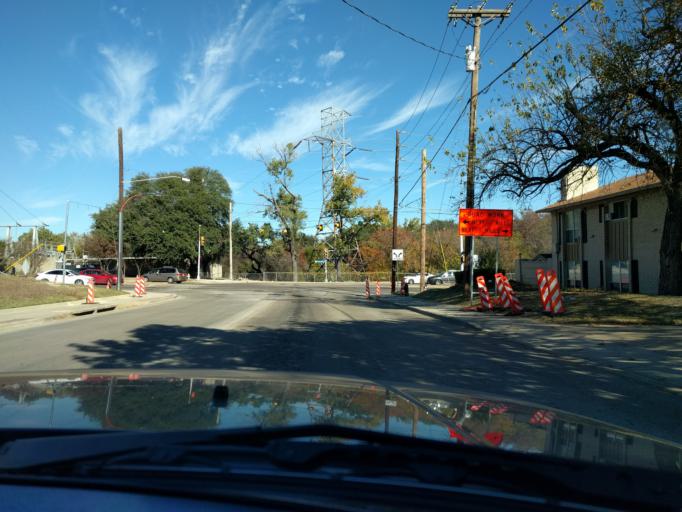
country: US
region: Texas
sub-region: Dallas County
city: Richardson
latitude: 32.9395
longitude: -96.7611
